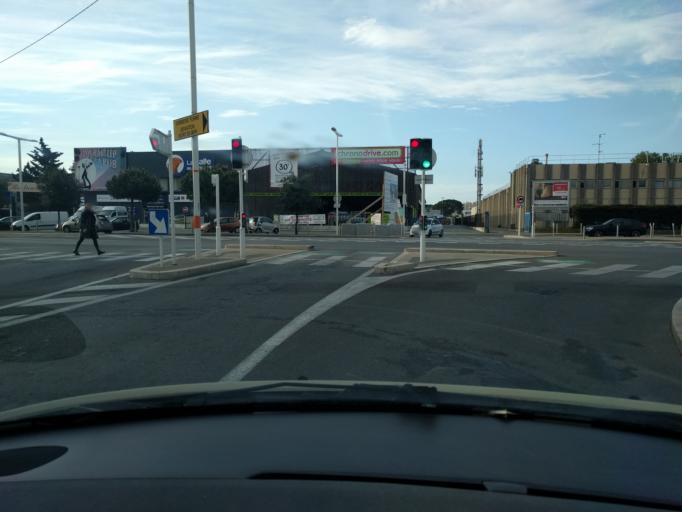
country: FR
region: Provence-Alpes-Cote d'Azur
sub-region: Departement des Alpes-Maritimes
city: Mandelieu-la-Napoule
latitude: 43.5502
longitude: 6.9661
